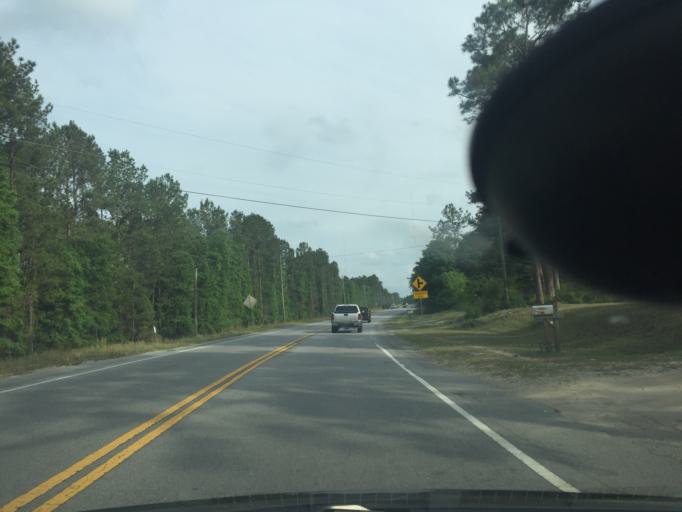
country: US
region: Georgia
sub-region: Chatham County
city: Bloomingdale
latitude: 32.0718
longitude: -81.3606
